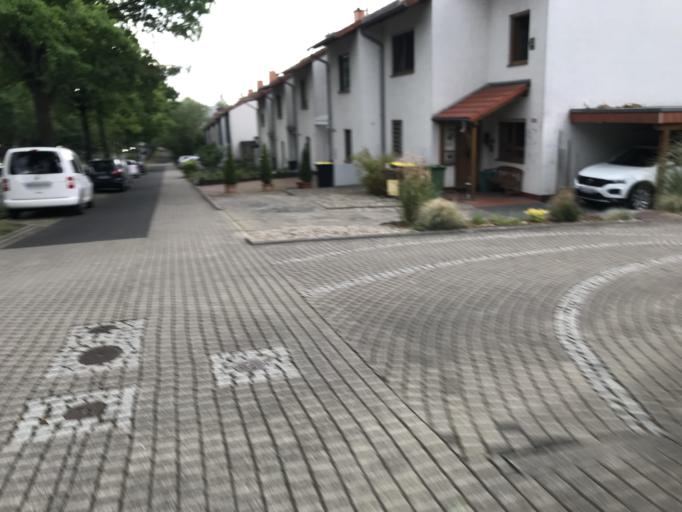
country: DE
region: Hesse
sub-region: Regierungsbezirk Kassel
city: Fuldabruck
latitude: 51.2908
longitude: 9.4485
